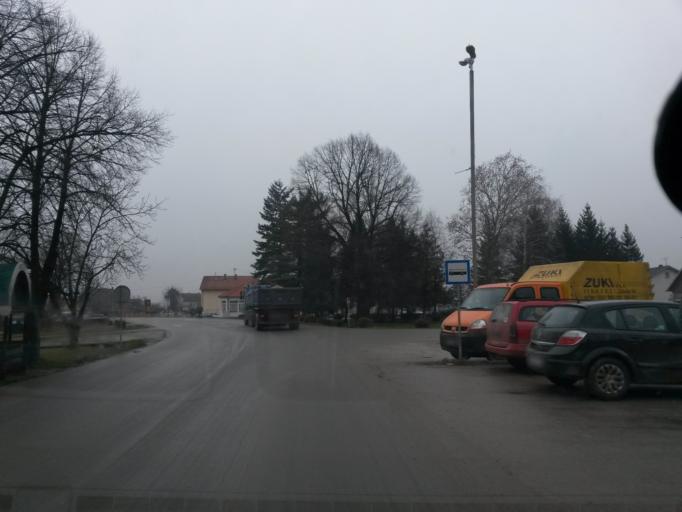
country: BA
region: Brcko
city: Brcko
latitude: 44.8874
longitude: 18.8252
